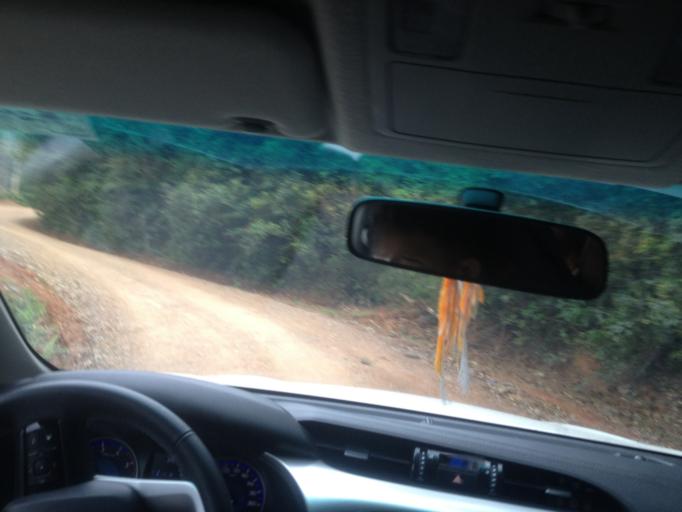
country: TH
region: Nan
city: Chaloem Phra Kiat
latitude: 19.9778
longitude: 101.1371
